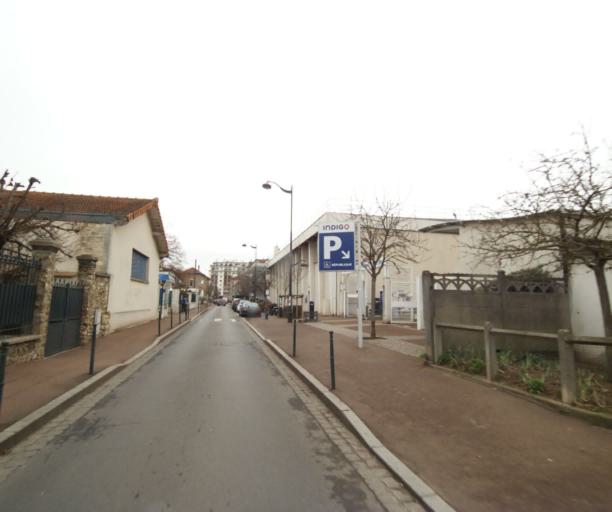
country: FR
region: Ile-de-France
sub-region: Departement des Hauts-de-Seine
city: Rueil-Malmaison
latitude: 48.8803
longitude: 2.1752
